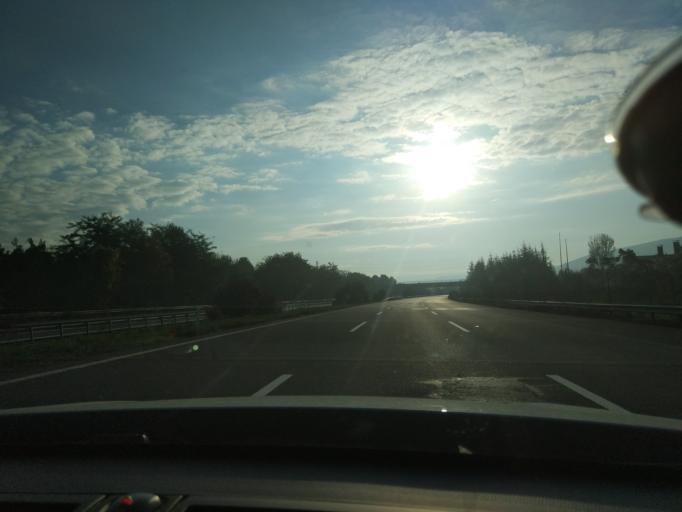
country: TR
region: Duzce
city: Duzce
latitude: 40.8035
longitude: 31.1714
